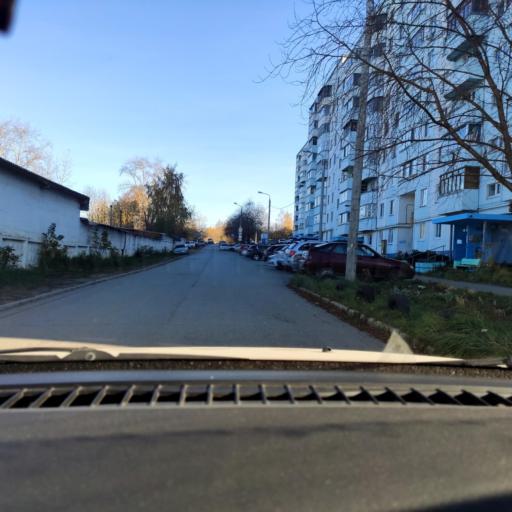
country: RU
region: Perm
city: Perm
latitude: 58.1141
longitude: 56.3741
